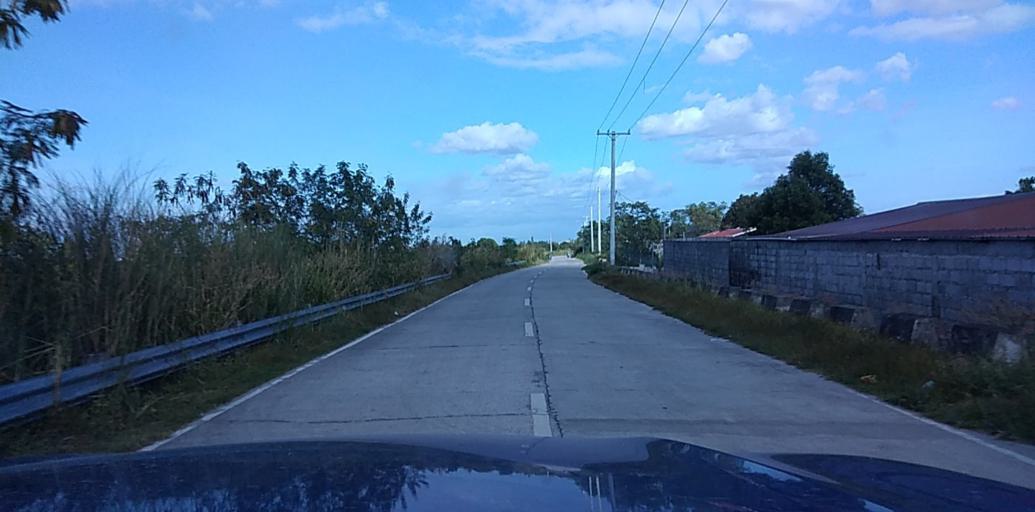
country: PH
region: Central Luzon
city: Santol
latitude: 15.1494
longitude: 120.5384
